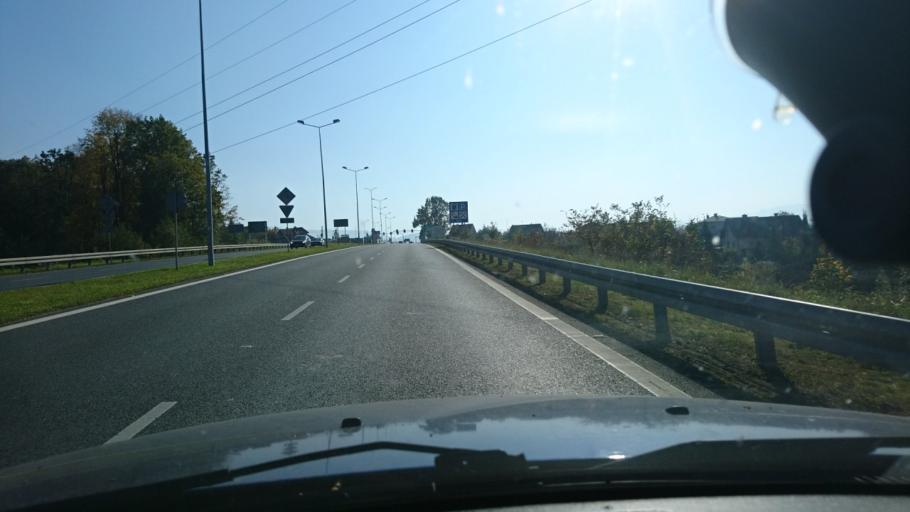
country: PL
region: Silesian Voivodeship
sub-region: Bielsko-Biala
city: Bielsko-Biala
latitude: 49.8413
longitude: 19.0697
